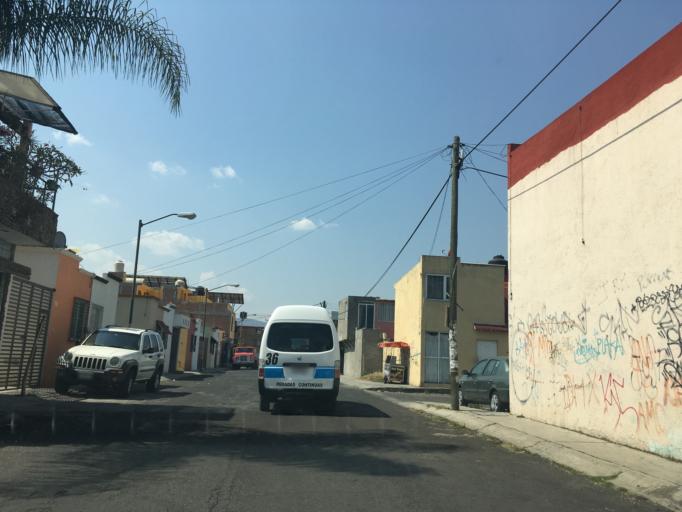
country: MX
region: Michoacan
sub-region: Morelia
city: Morelos
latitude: 19.6734
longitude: -101.2252
